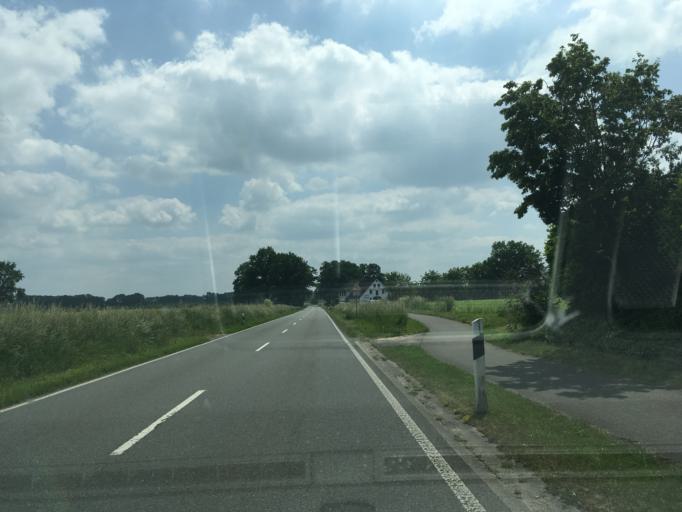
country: DE
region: North Rhine-Westphalia
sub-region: Regierungsbezirk Munster
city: Borken
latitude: 51.8285
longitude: 6.7794
